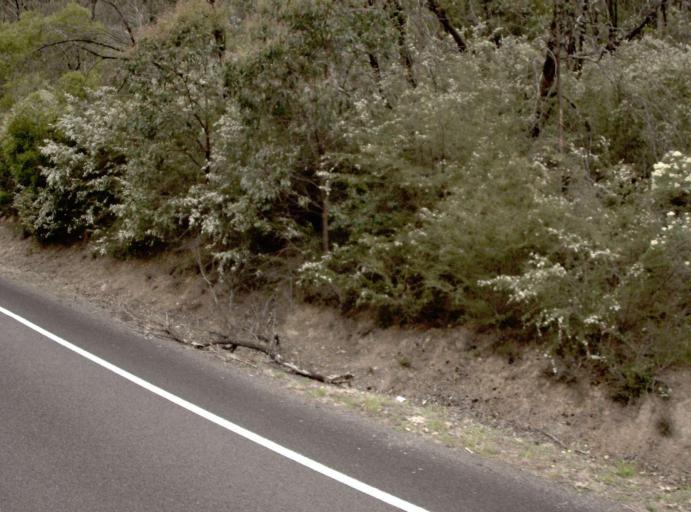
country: AU
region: New South Wales
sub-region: Bombala
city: Bombala
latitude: -37.2525
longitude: 149.2477
